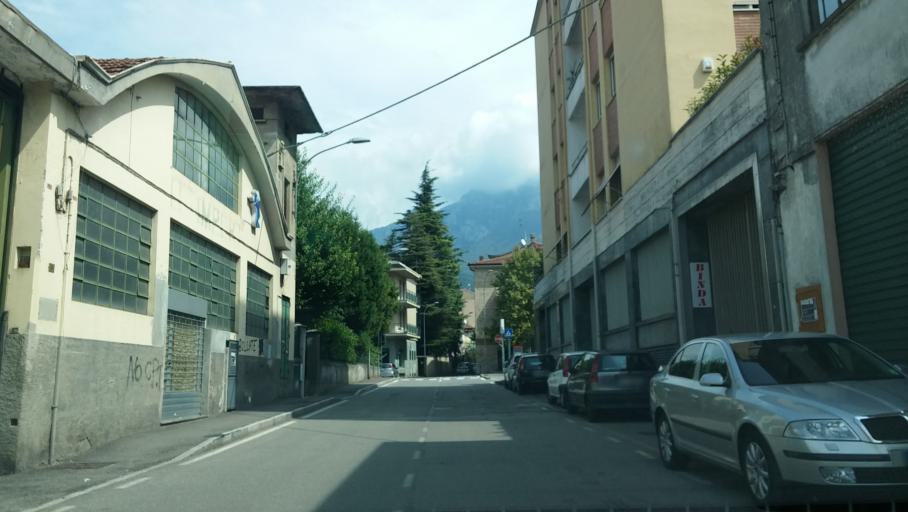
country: IT
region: Lombardy
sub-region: Provincia di Lecco
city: Pescate
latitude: 45.8442
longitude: 9.3996
